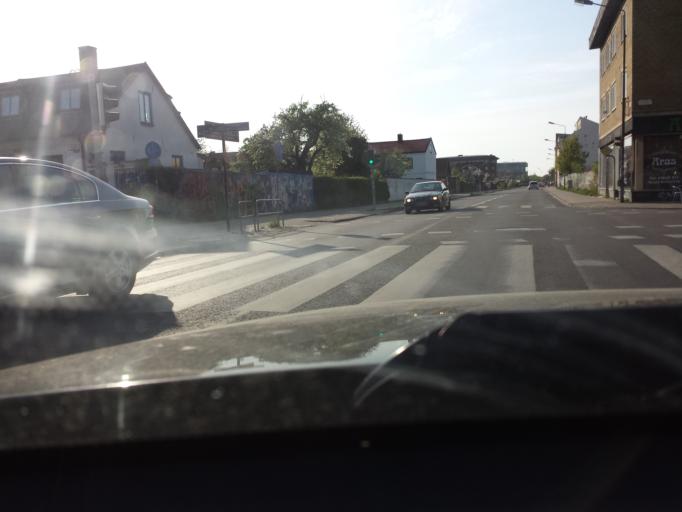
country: SE
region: Skane
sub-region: Malmo
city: Malmoe
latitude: 55.5856
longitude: 13.0153
